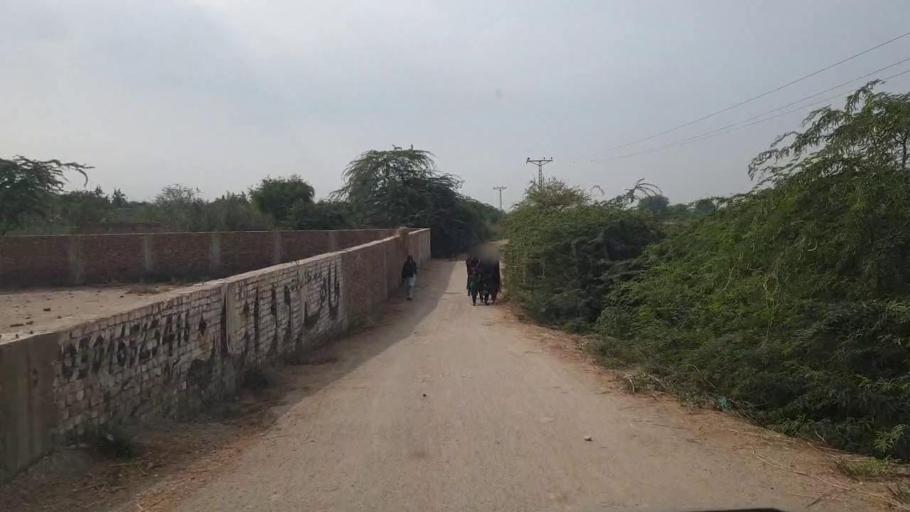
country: PK
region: Sindh
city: Talhar
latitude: 24.8871
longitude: 68.8024
